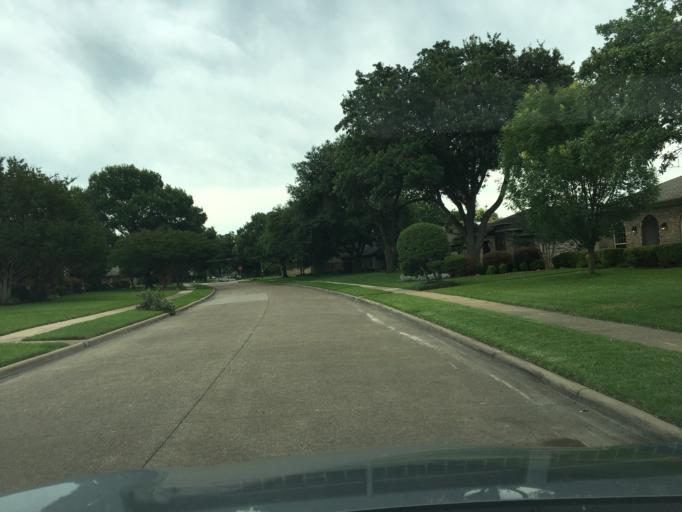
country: US
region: Texas
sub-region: Dallas County
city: Richardson
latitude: 32.9416
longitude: -96.7112
